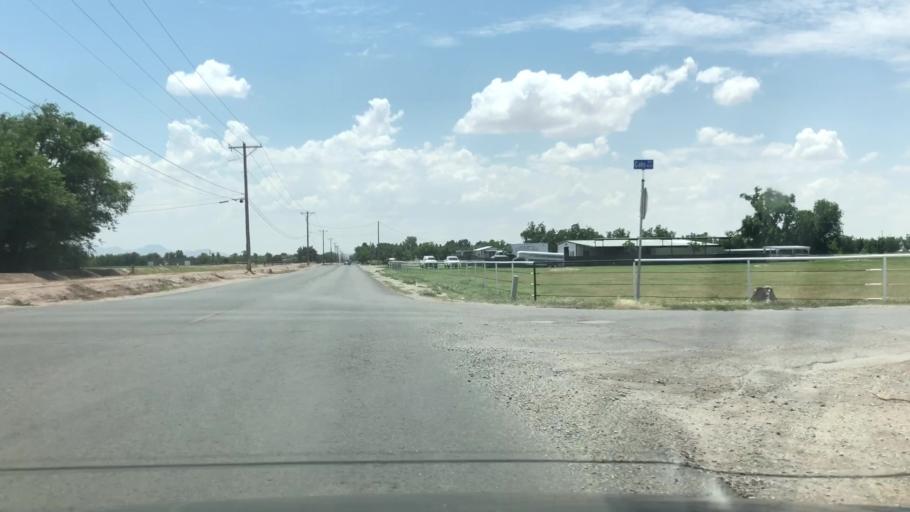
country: US
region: Texas
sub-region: El Paso County
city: Canutillo
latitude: 31.9092
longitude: -106.6251
